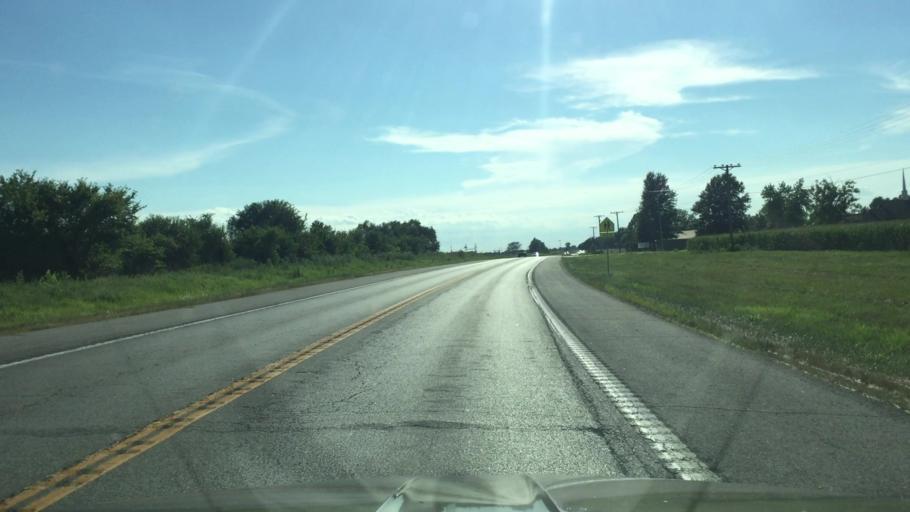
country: US
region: Missouri
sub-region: Pettis County
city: Sedalia
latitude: 38.6946
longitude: -93.1404
